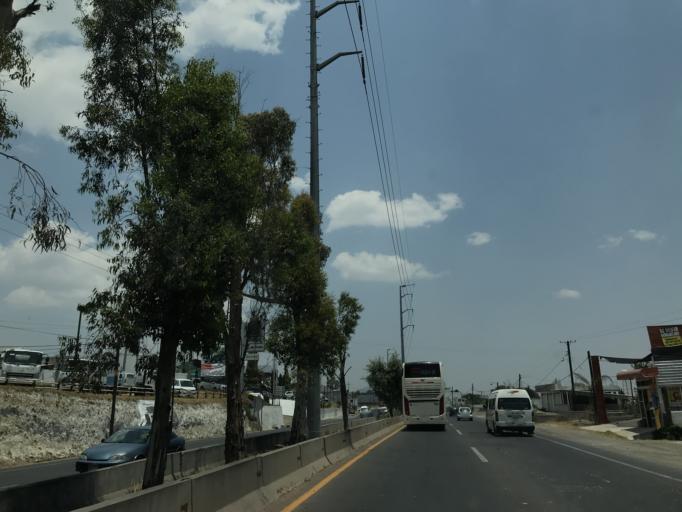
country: MX
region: Tlaxcala
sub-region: Yauhquemehcan
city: Hualcaltzinco
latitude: 19.4099
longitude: -98.1679
